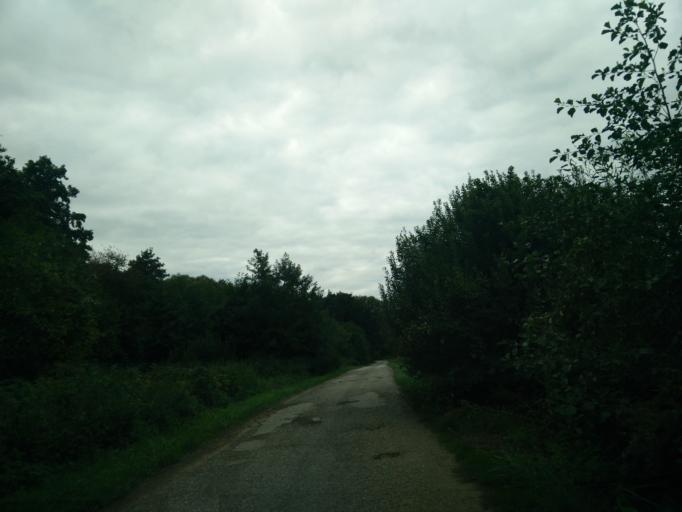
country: SK
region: Nitriansky
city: Novaky
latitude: 48.6361
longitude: 18.4935
